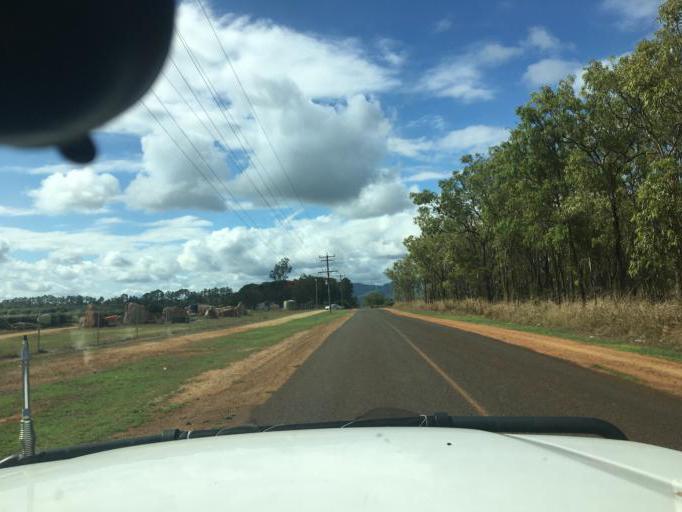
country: AU
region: Queensland
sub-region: Tablelands
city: Mareeba
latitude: -17.1017
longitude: 145.4116
